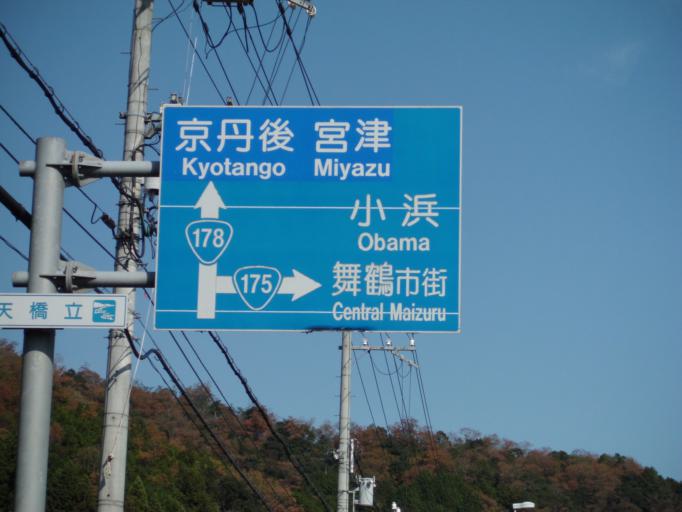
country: JP
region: Kyoto
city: Maizuru
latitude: 35.4516
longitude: 135.2646
